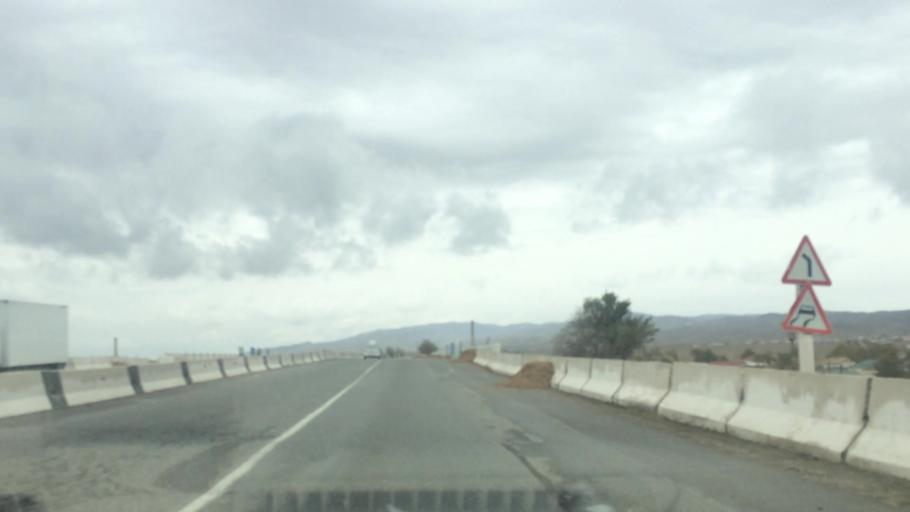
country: UZ
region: Samarqand
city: Bulung'ur
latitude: 39.8373
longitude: 67.4377
